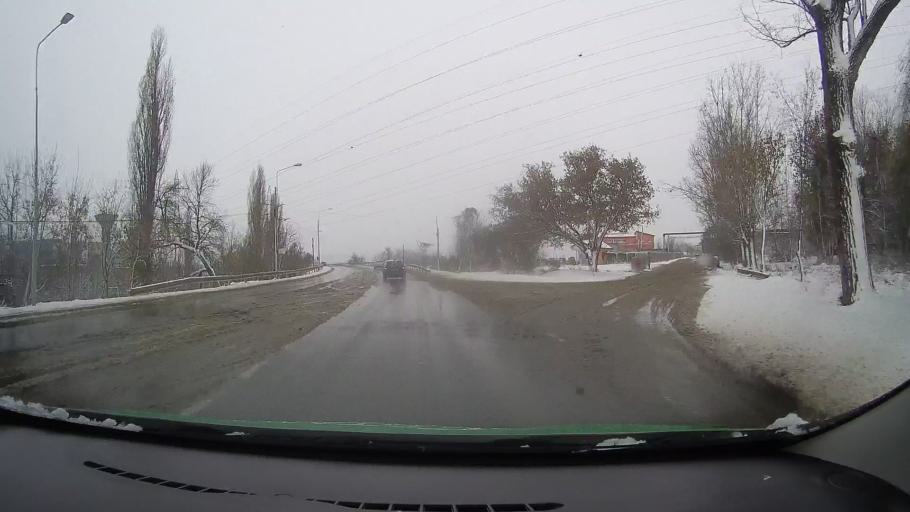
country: RO
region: Hunedoara
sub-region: Municipiul Hunedoara
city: Pestisu Mare
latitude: 45.7855
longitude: 22.9108
